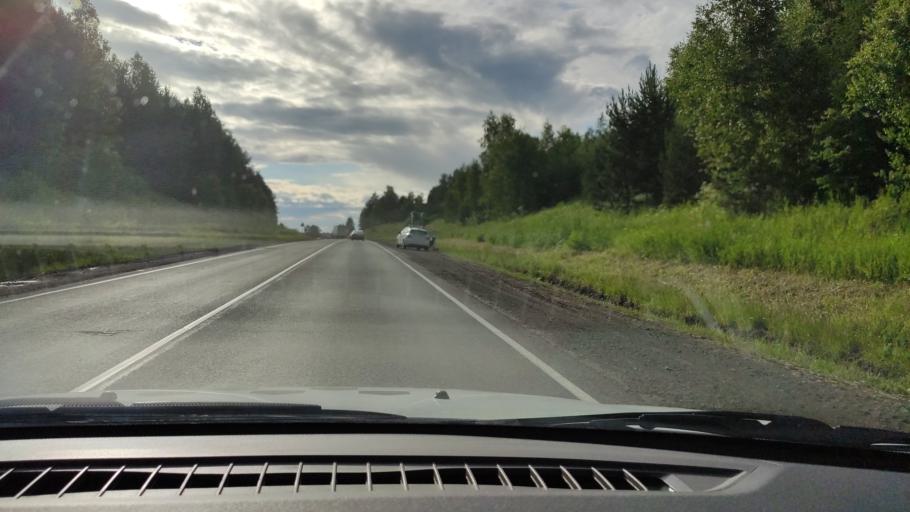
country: RU
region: Perm
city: Kukushtan
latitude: 57.4830
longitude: 56.6940
